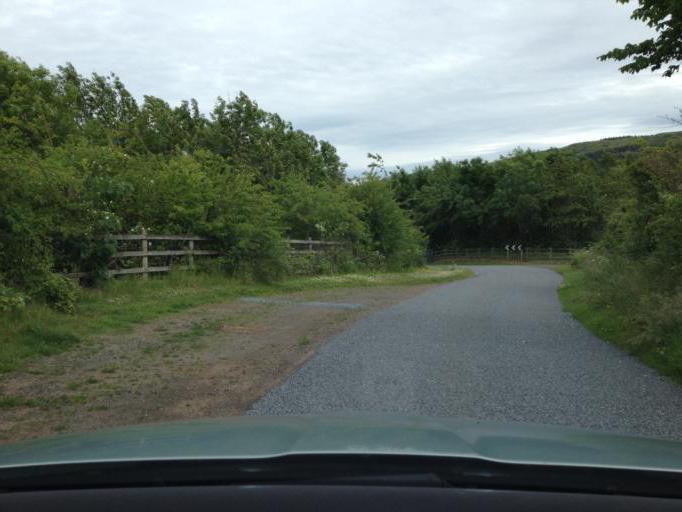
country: GB
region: Scotland
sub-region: Perth and Kinross
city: Bridge of Earn
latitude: 56.3271
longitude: -3.3998
